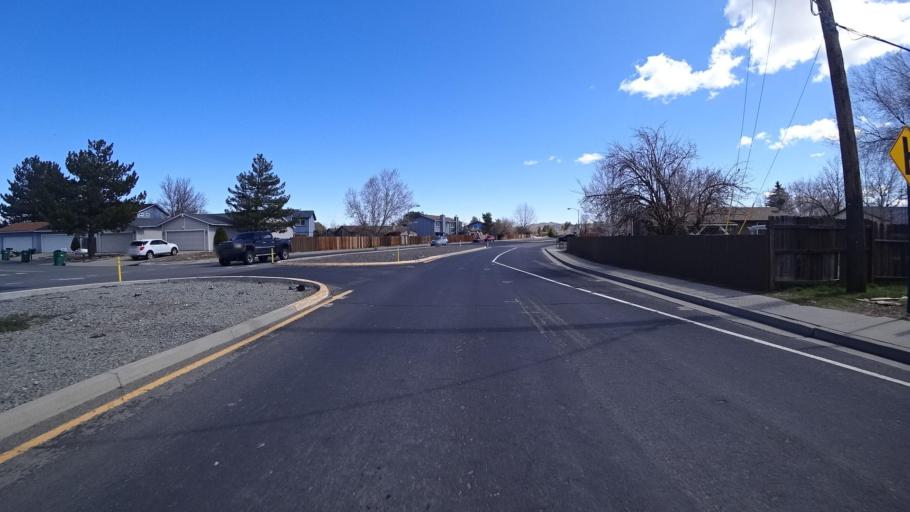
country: US
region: Nevada
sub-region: Washoe County
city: Lemmon Valley
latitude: 39.6423
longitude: -119.8791
